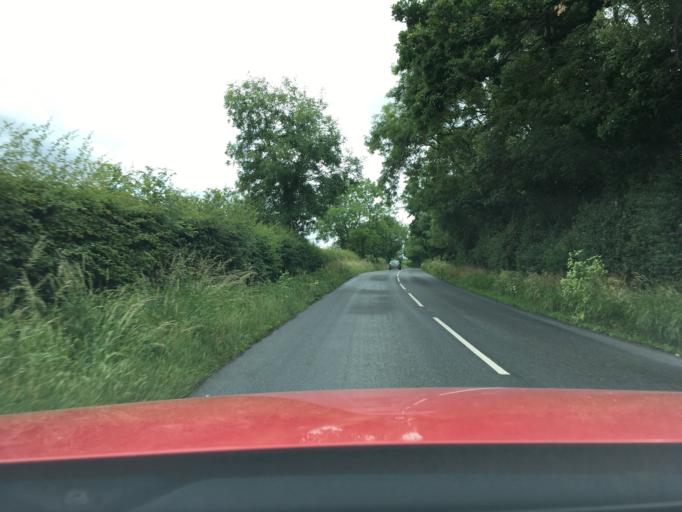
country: GB
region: England
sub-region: Gloucestershire
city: Winchcombe
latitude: 52.0198
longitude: -1.9598
